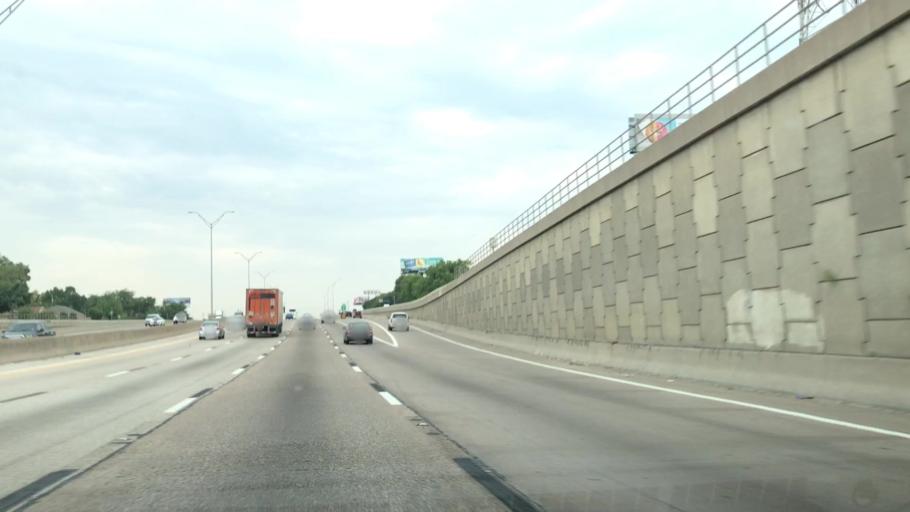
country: US
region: Texas
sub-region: Tarrant County
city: Fort Worth
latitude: 32.7132
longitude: -97.3207
